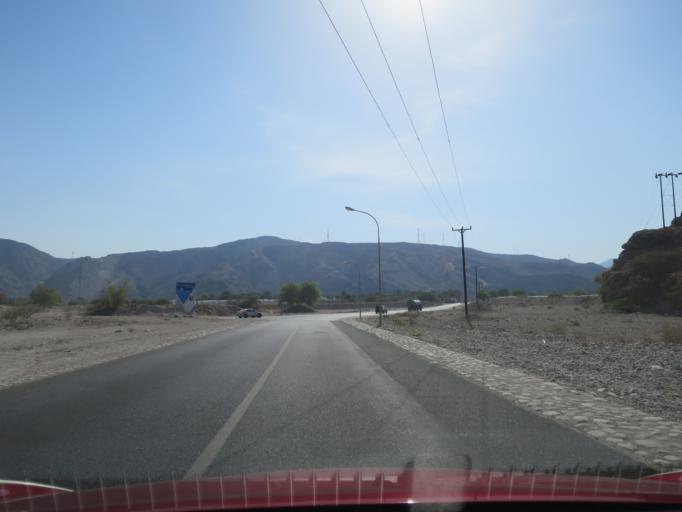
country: OM
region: Muhafazat Masqat
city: Muscat
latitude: 23.5087
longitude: 58.6599
